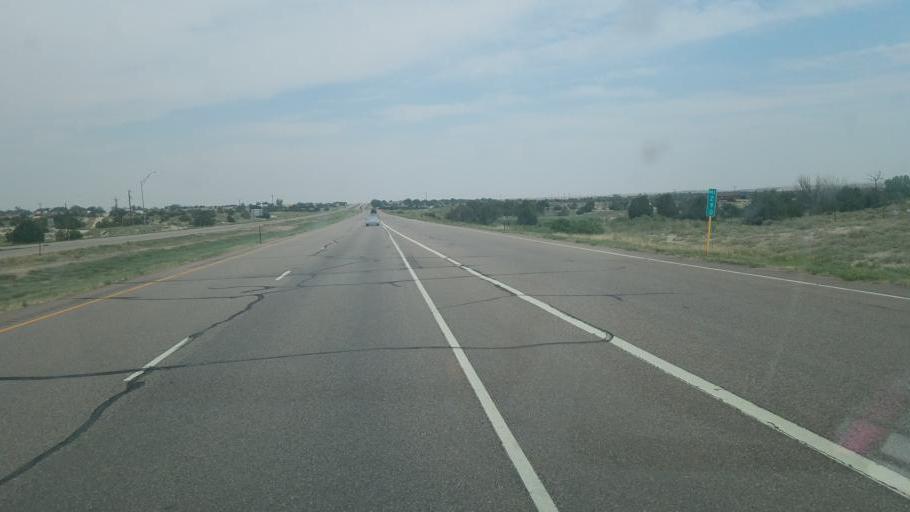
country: US
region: Colorado
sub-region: Fremont County
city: Penrose
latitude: 38.4175
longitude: -105.0386
